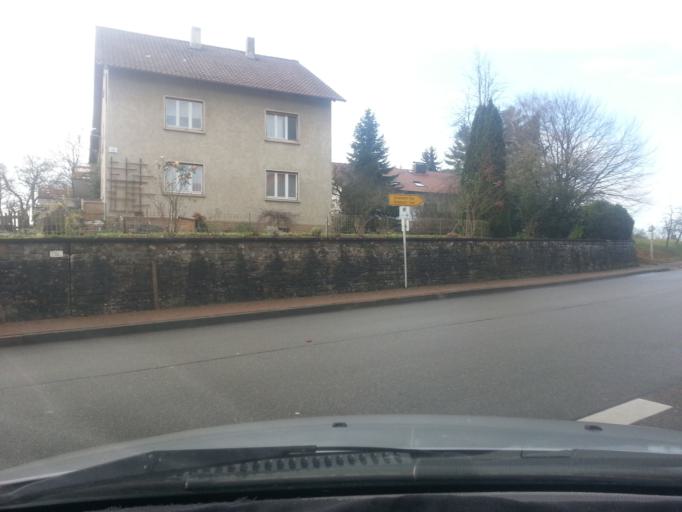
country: DE
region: Baden-Wuerttemberg
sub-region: Regierungsbezirk Stuttgart
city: Eppingen
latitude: 49.1697
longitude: 8.8886
